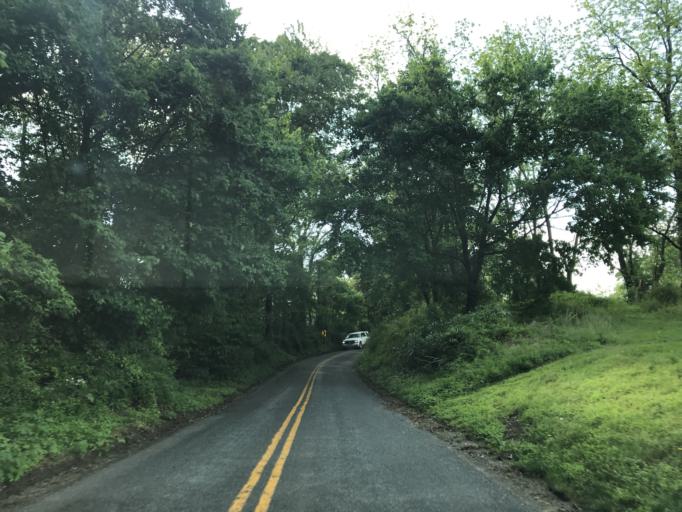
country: US
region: Maryland
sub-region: Harford County
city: Bel Air North
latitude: 39.5744
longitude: -76.3984
